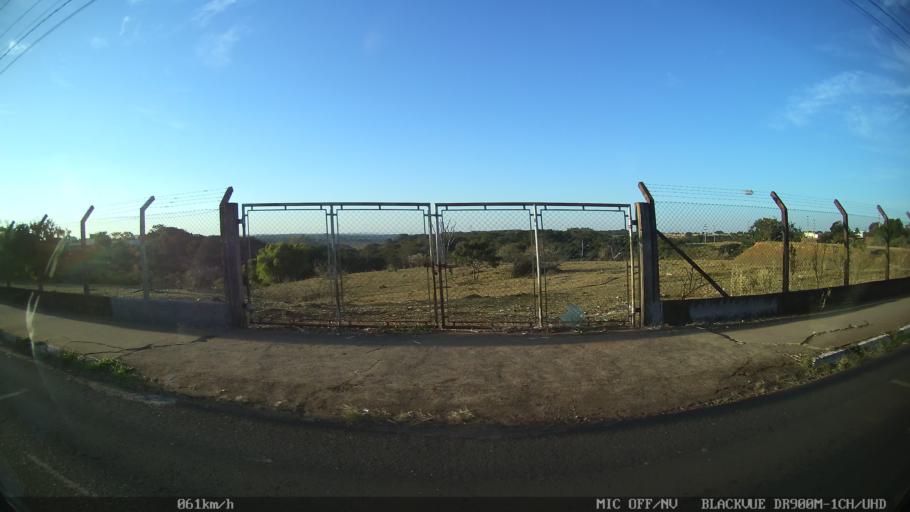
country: BR
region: Sao Paulo
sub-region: Franca
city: Franca
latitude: -20.5128
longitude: -47.3833
